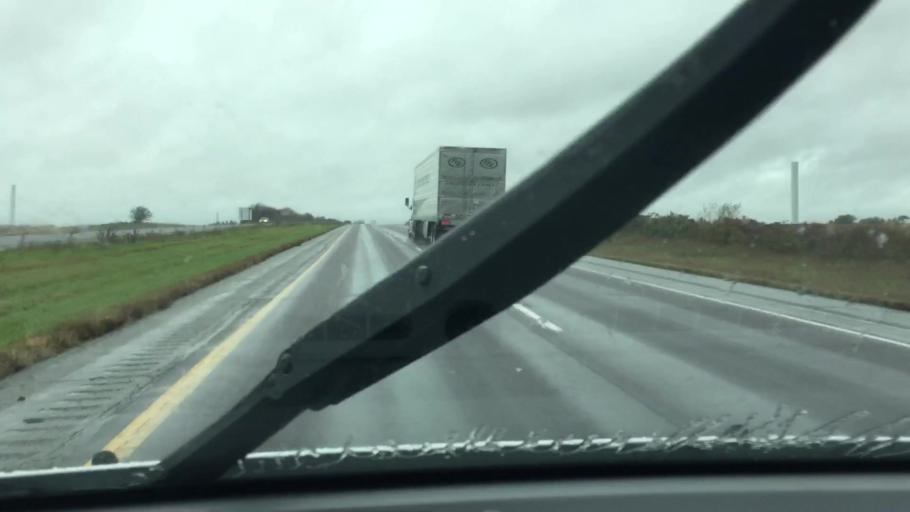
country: US
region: Iowa
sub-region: Poweshiek County
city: Montezuma
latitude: 41.6962
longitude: -92.5744
